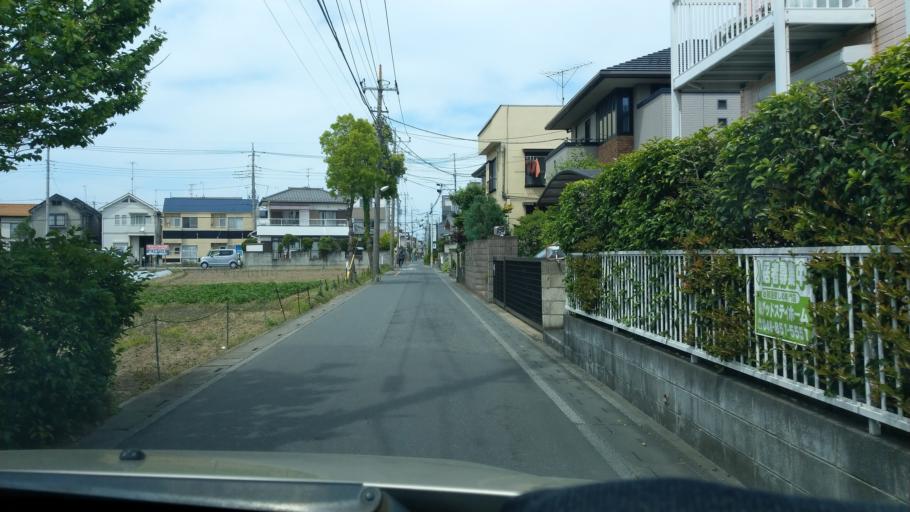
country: JP
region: Saitama
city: Yono
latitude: 35.8637
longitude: 139.6123
